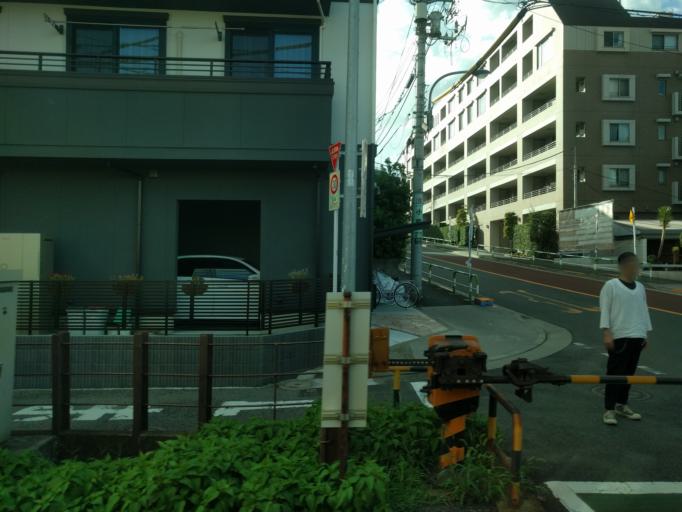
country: JP
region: Saitama
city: Kawaguchi
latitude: 35.7471
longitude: 139.7351
